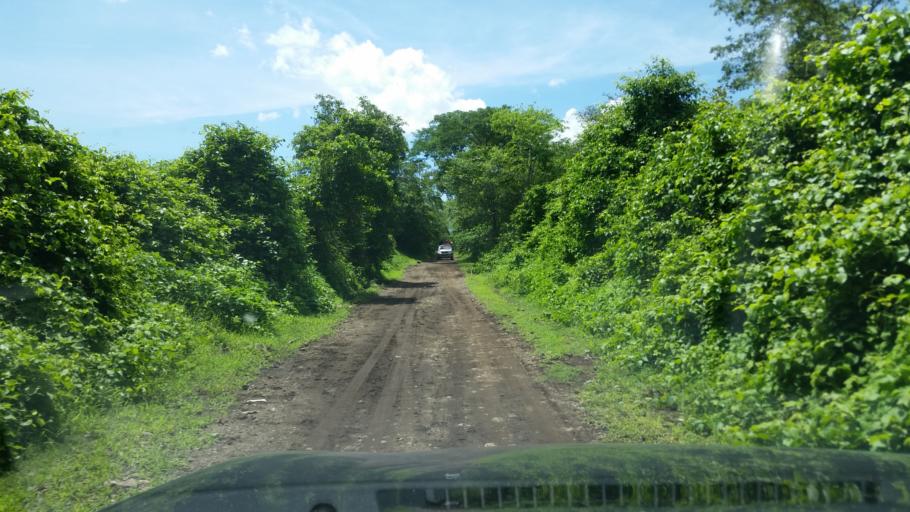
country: NI
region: Chinandega
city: Puerto Morazan
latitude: 12.7611
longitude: -87.1300
